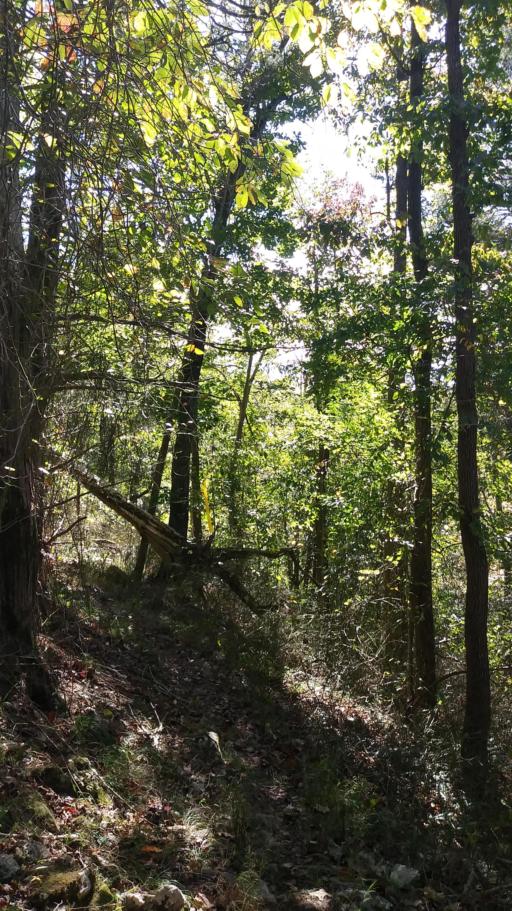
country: US
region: Maryland
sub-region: Cecil County
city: Rising Sun
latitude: 39.7011
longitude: -76.1807
